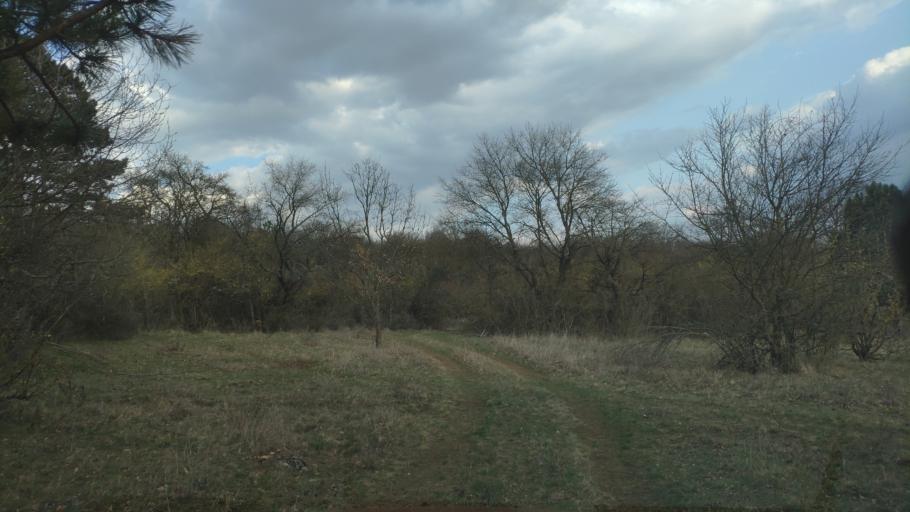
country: SK
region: Kosicky
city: Medzev
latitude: 48.6198
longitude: 20.9115
